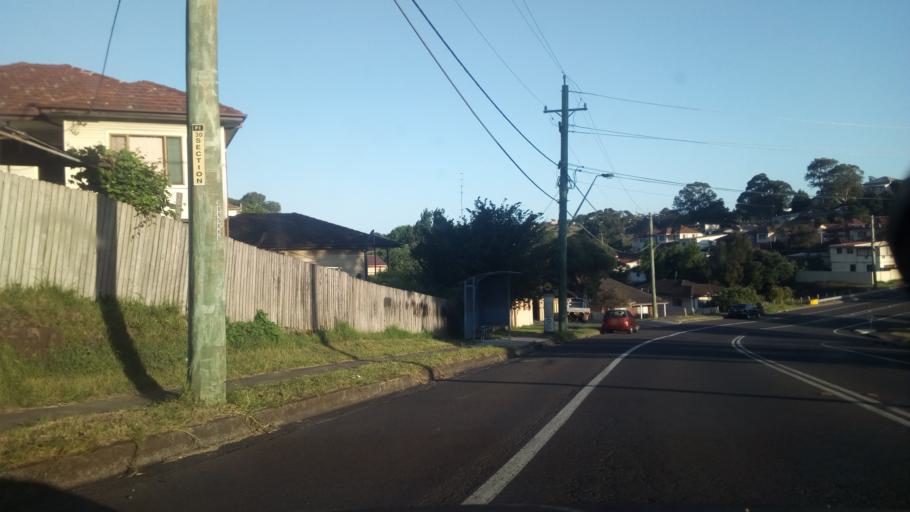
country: AU
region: New South Wales
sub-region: Wollongong
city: Lake Heights
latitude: -34.4740
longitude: 150.8718
